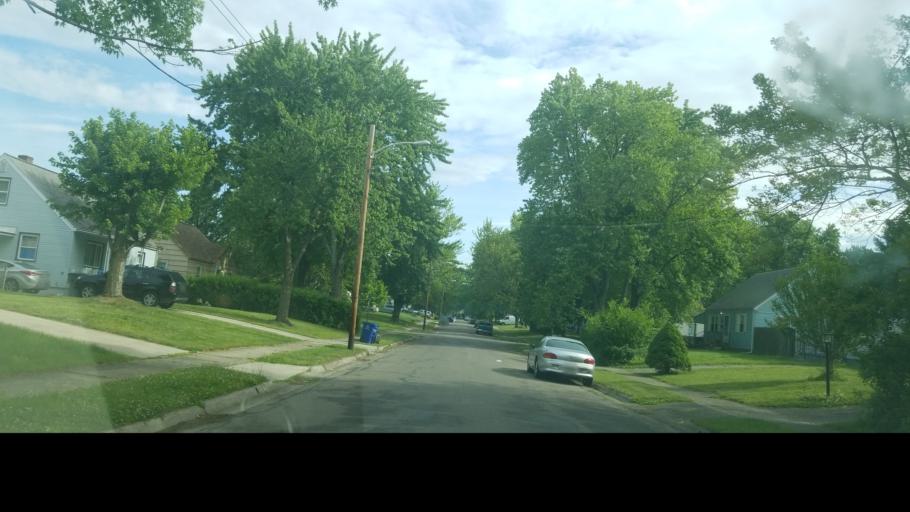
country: US
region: Ohio
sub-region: Franklin County
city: Minerva Park
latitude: 40.0377
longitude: -82.9717
